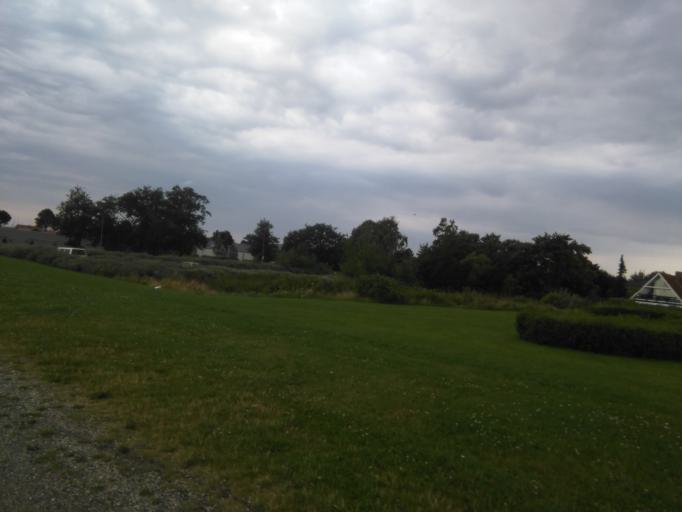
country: DK
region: Central Jutland
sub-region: Arhus Kommune
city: Hjortshoj
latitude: 56.2037
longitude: 10.2829
